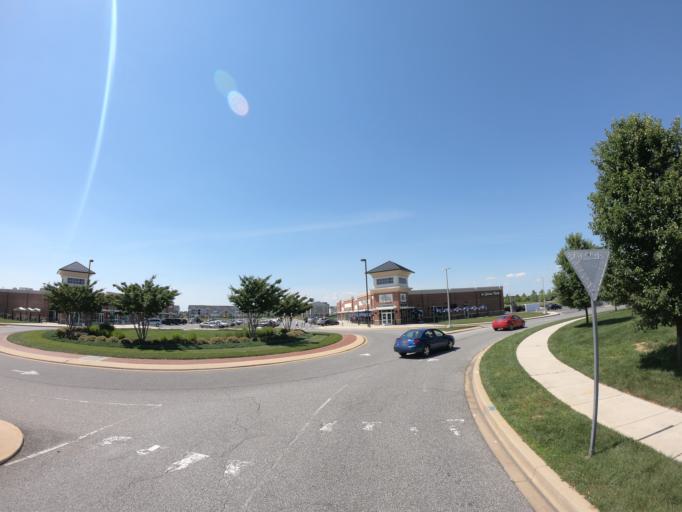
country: US
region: Delaware
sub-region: New Castle County
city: Middletown
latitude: 39.4481
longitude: -75.7320
